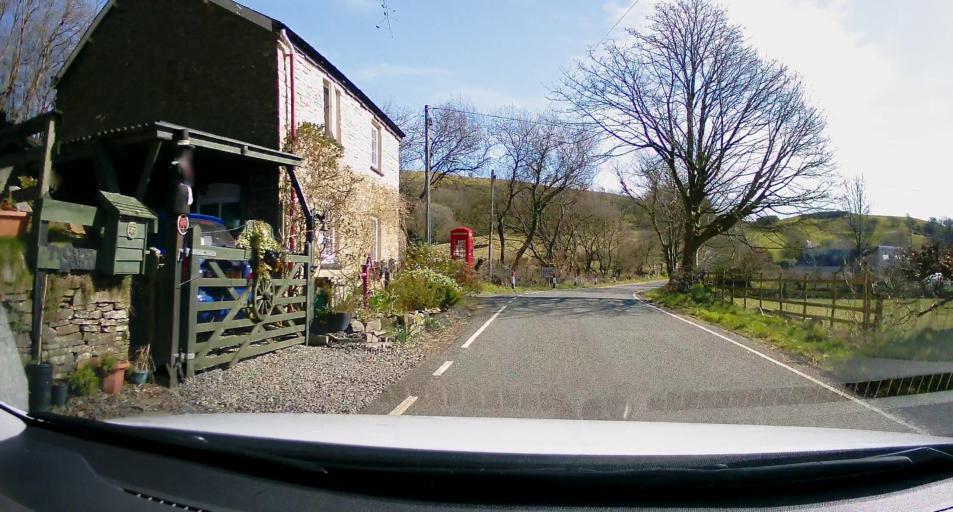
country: GB
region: Wales
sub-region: County of Ceredigion
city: Lledrod
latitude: 52.2836
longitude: -4.0598
